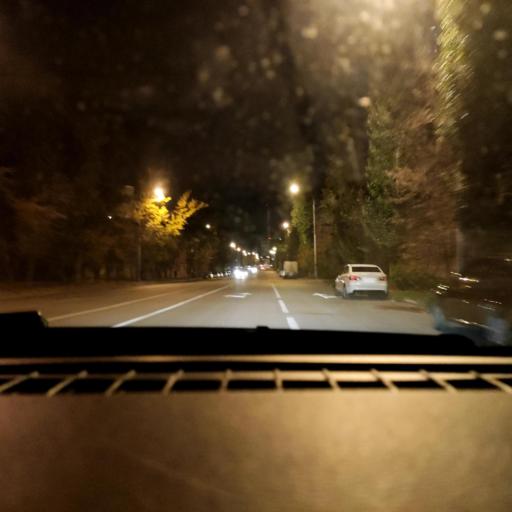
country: RU
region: Voronezj
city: Maslovka
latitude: 51.6215
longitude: 39.2421
